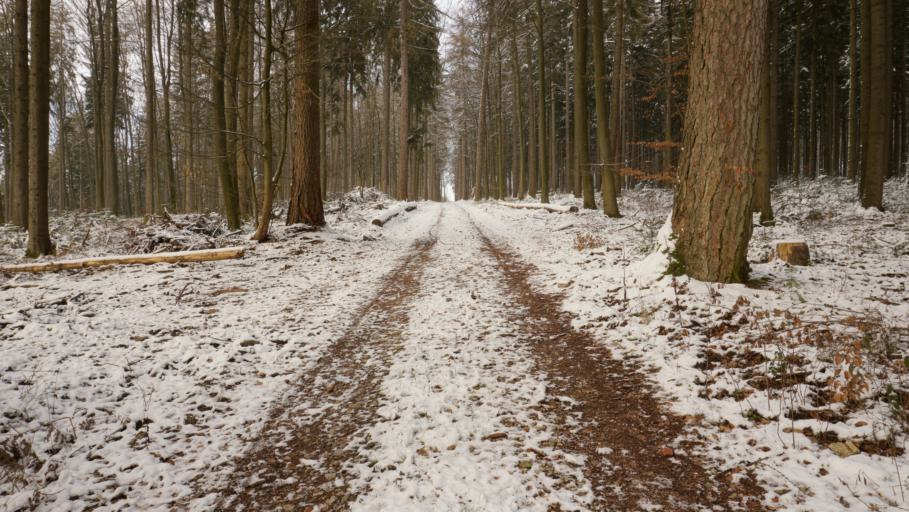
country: DE
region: Baden-Wuerttemberg
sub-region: Karlsruhe Region
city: Neckargerach
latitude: 49.4294
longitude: 9.0988
